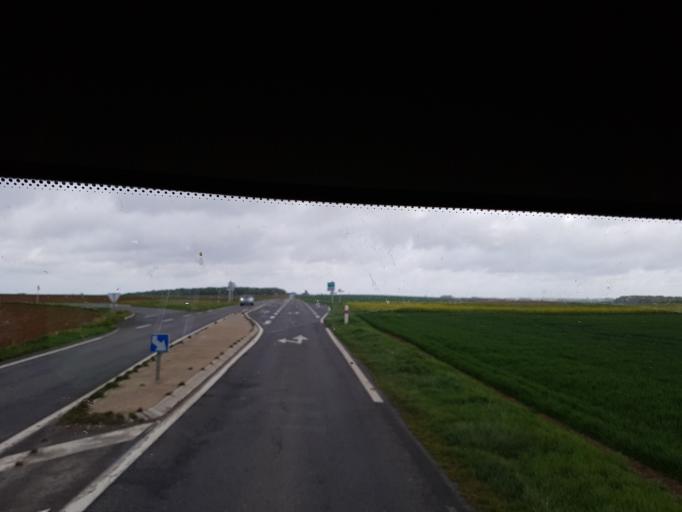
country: FR
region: Picardie
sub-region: Departement de l'Aisne
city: Crouy
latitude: 49.4266
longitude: 3.3498
